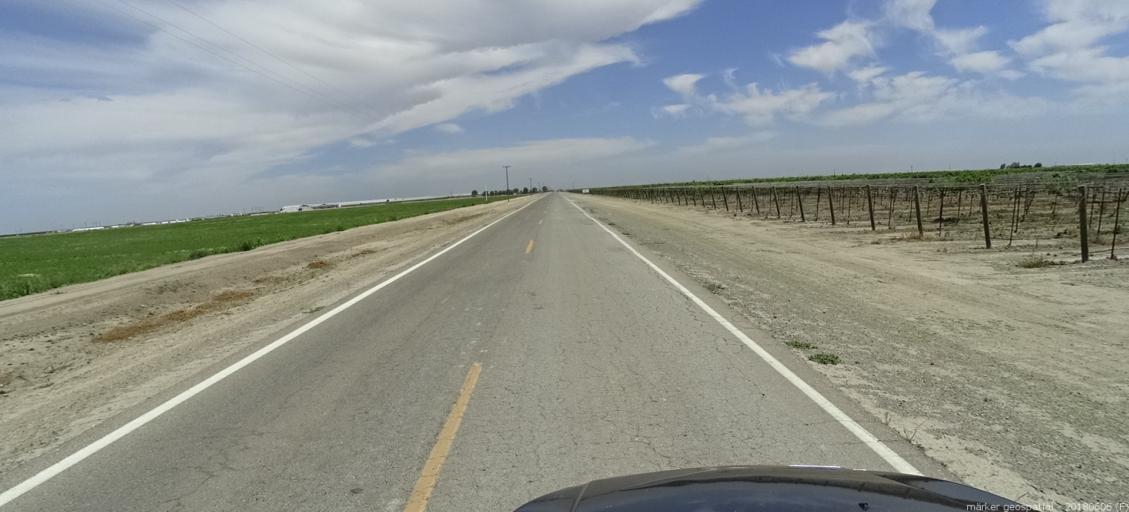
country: US
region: California
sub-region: Fresno County
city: Firebaugh
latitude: 36.9250
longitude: -120.3822
